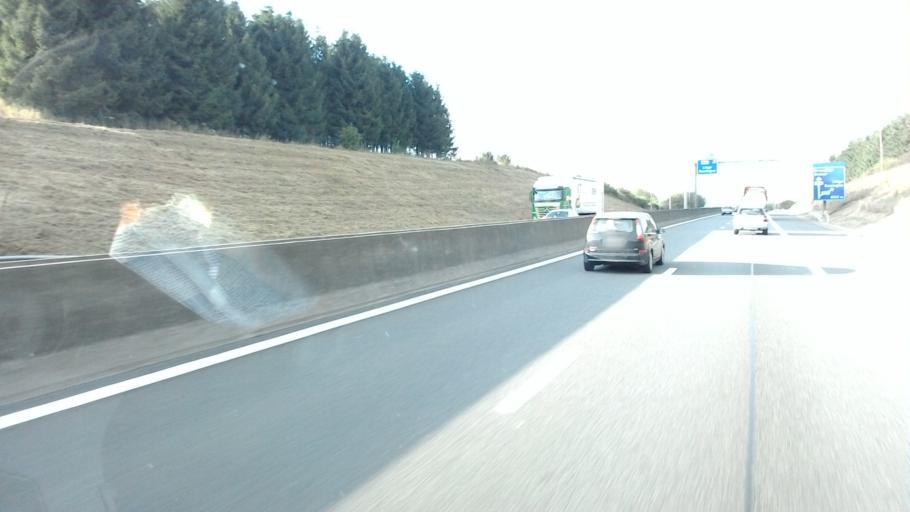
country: BE
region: Wallonia
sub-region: Province du Luxembourg
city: Leglise
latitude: 49.8455
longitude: 5.5108
